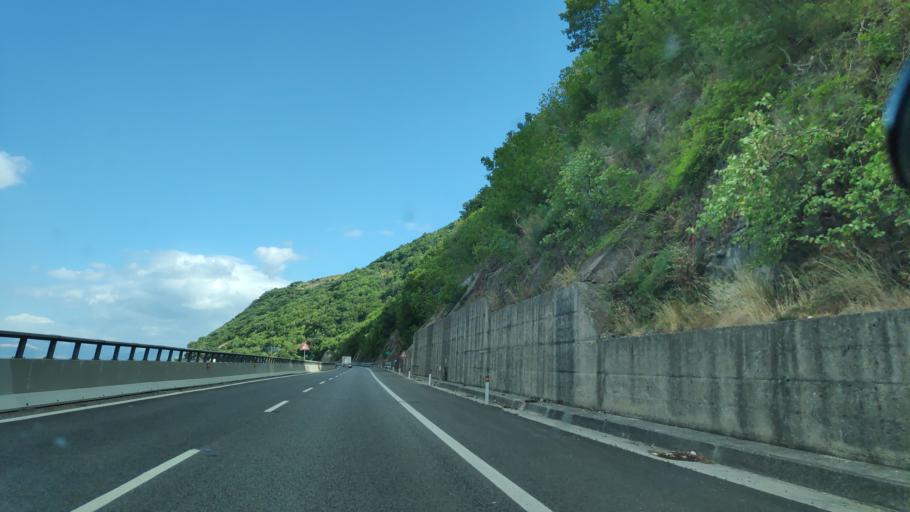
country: IT
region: Campania
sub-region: Provincia di Salerno
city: Sicignano degli Alburni
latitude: 40.5949
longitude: 15.3223
